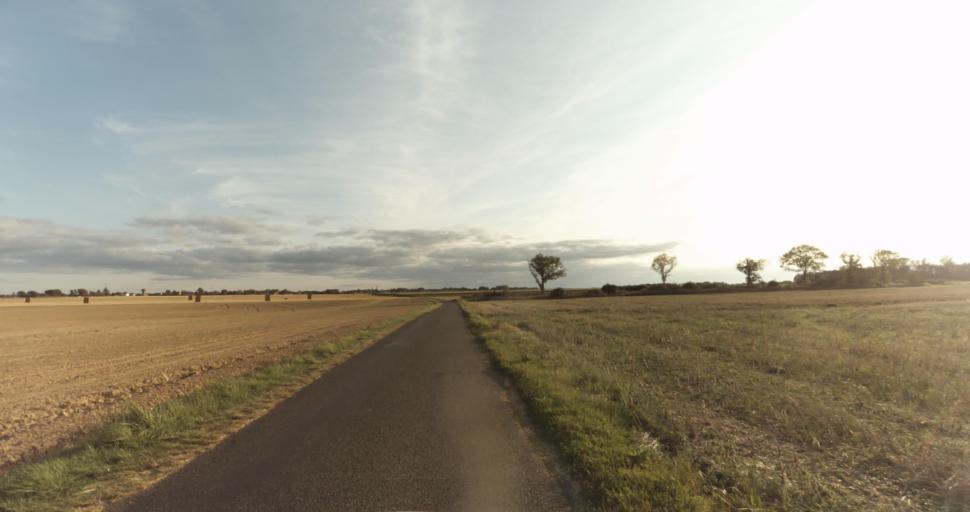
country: FR
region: Haute-Normandie
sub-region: Departement de l'Eure
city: Saint-Germain-sur-Avre
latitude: 48.8320
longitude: 1.2773
